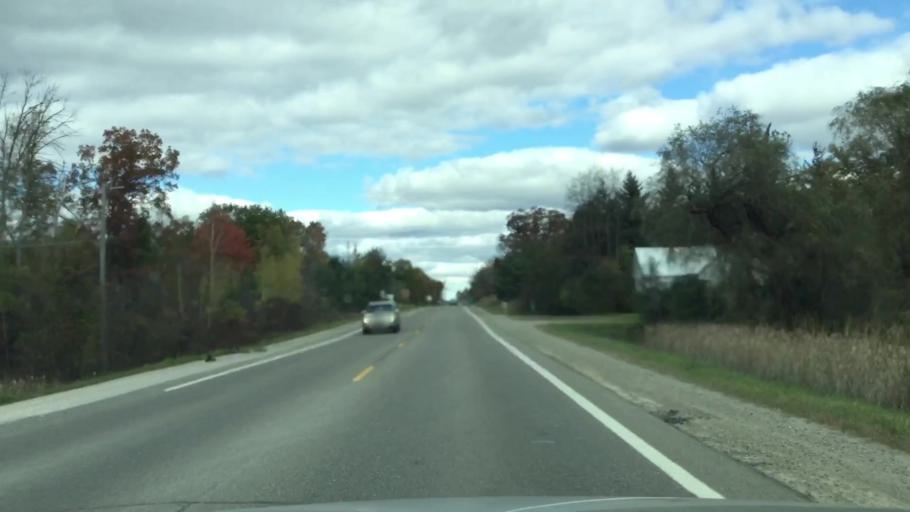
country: US
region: Michigan
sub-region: Lapeer County
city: Barnes Lake-Millers Lake
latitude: 43.1811
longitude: -83.3123
